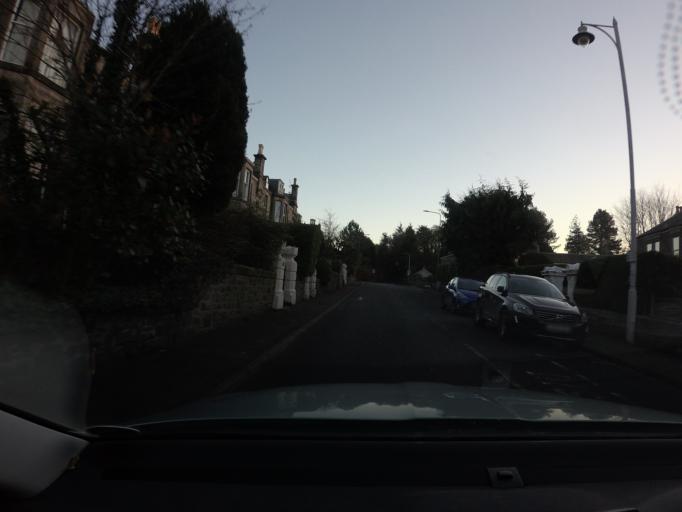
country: GB
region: Scotland
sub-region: Fife
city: Newport-On-Tay
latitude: 56.4389
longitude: -2.9380
